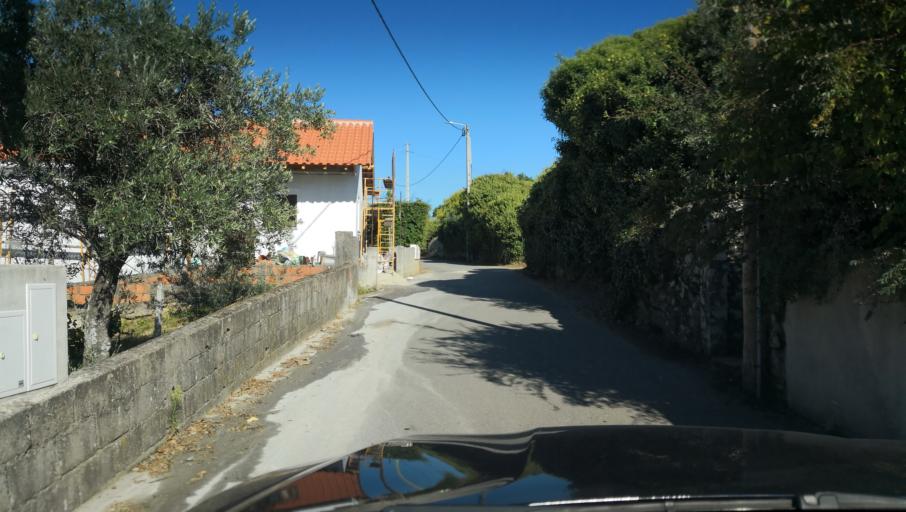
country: PT
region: Vila Real
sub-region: Vila Real
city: Vila Real
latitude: 41.2799
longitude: -7.7439
